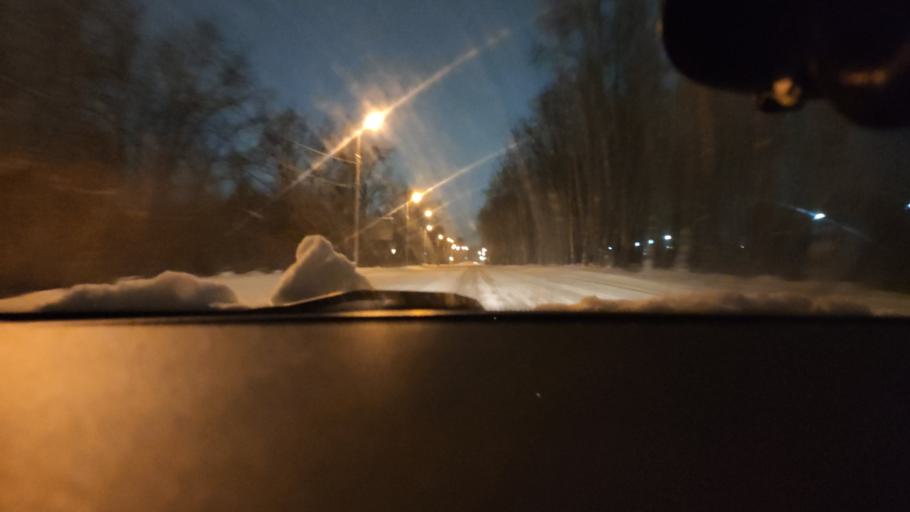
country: RU
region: Perm
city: Krasnokamsk
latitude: 58.0654
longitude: 55.7979
